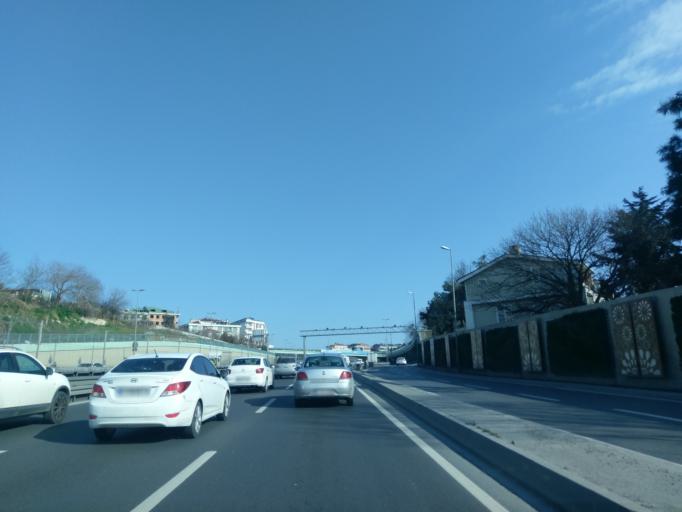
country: TR
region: Istanbul
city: Mahmutbey
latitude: 40.9860
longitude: 28.7758
